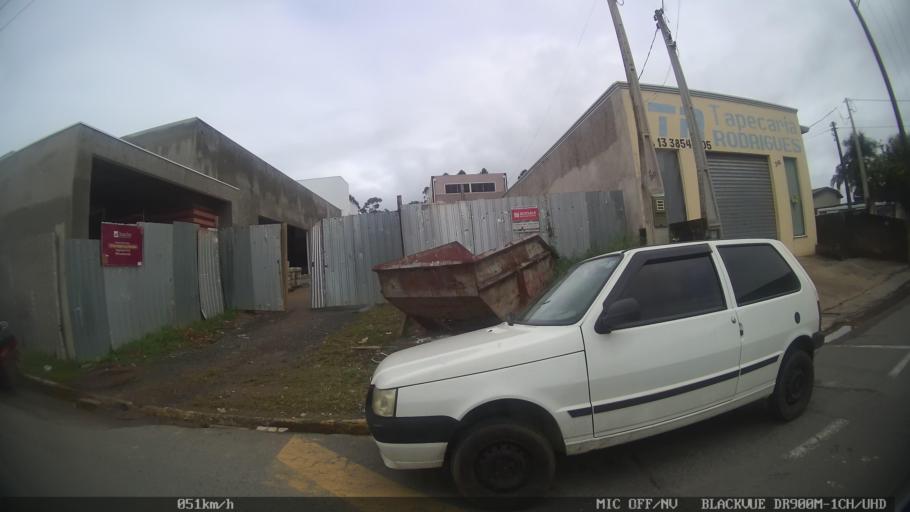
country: BR
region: Sao Paulo
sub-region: Cajati
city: Cajati
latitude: -24.7288
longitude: -48.1046
